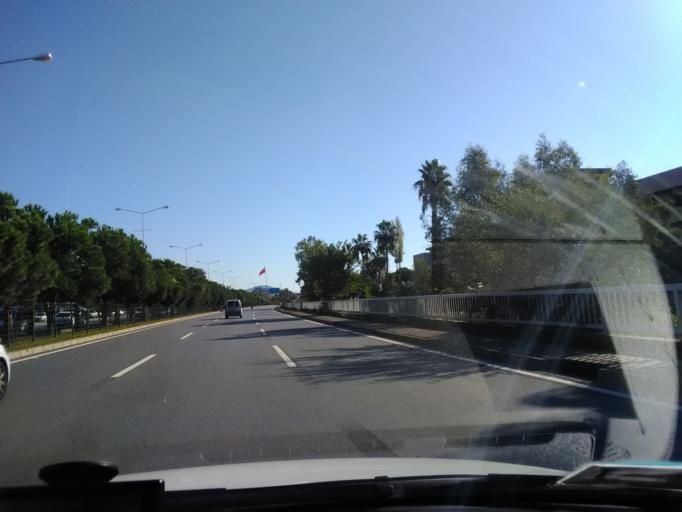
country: TR
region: Antalya
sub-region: Alanya
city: Mahmutlar
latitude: 36.5206
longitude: 32.0575
